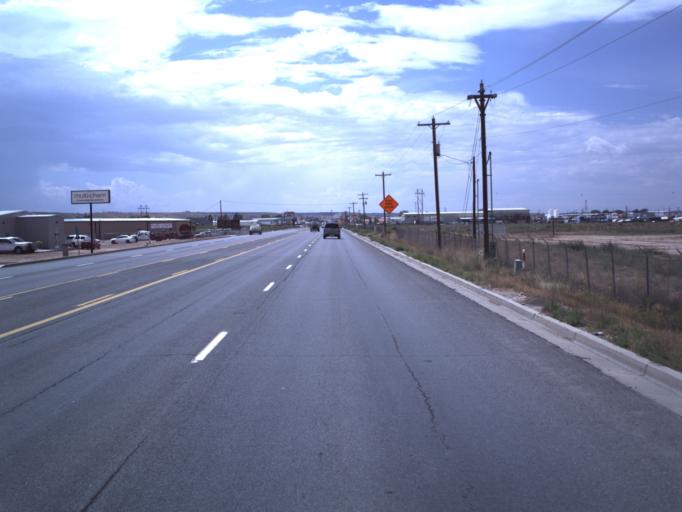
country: US
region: Utah
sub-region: Duchesne County
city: Roosevelt
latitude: 40.2786
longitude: -110.0204
